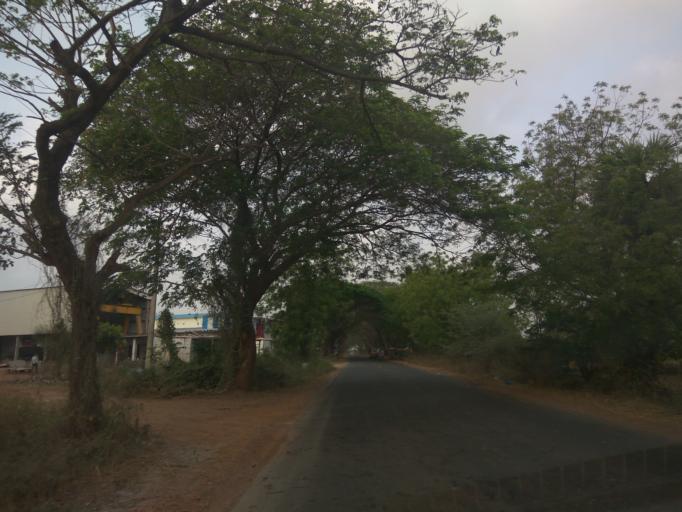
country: IN
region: Andhra Pradesh
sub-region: Prakasam
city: Kandukur
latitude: 15.2069
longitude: 79.8645
